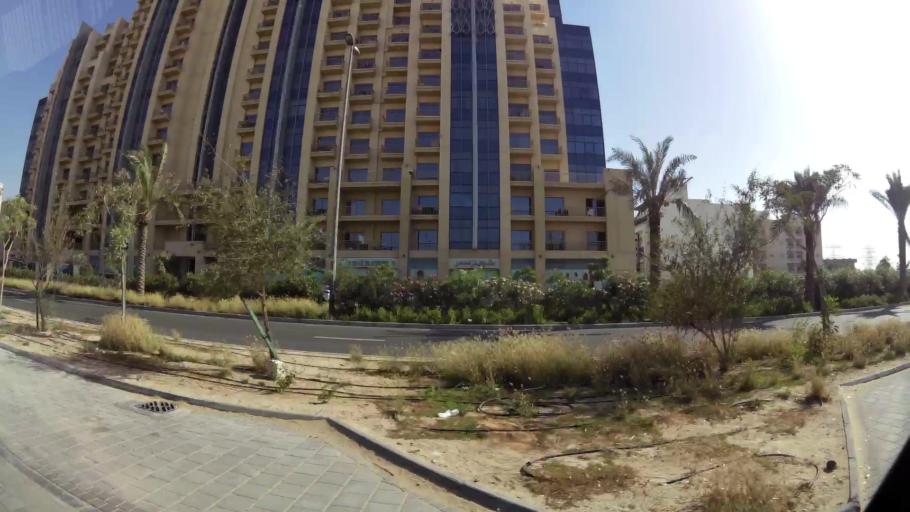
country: AE
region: Dubai
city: Dubai
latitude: 25.0695
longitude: 55.2074
